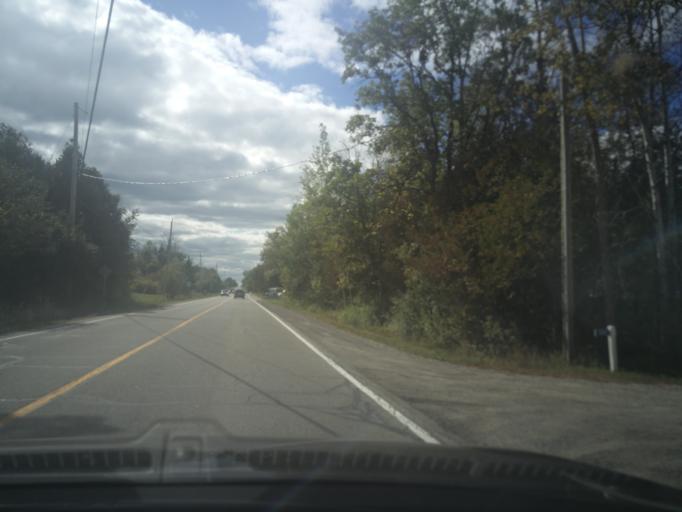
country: CA
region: Ontario
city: Carleton Place
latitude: 45.1025
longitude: -75.9740
